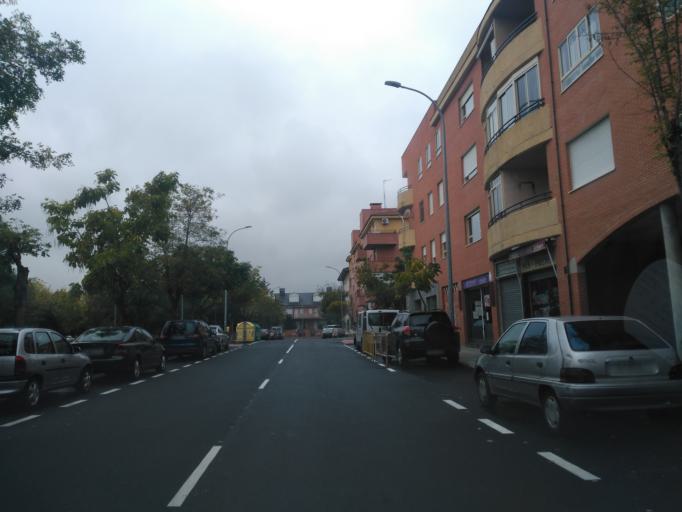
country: ES
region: Castille and Leon
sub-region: Provincia de Salamanca
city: Salamanca
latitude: 40.9556
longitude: -5.6878
